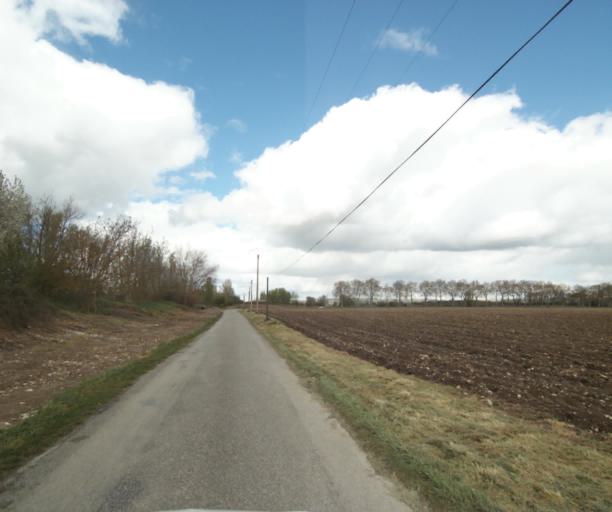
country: FR
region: Midi-Pyrenees
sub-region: Departement de l'Ariege
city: Saverdun
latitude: 43.2513
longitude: 1.5818
